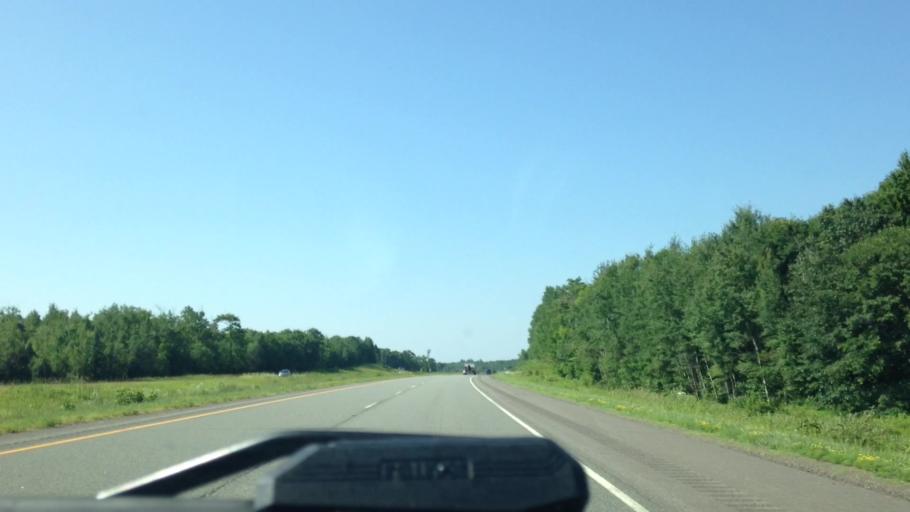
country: US
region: Wisconsin
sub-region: Douglas County
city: Lake Nebagamon
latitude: 46.4090
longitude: -91.8121
